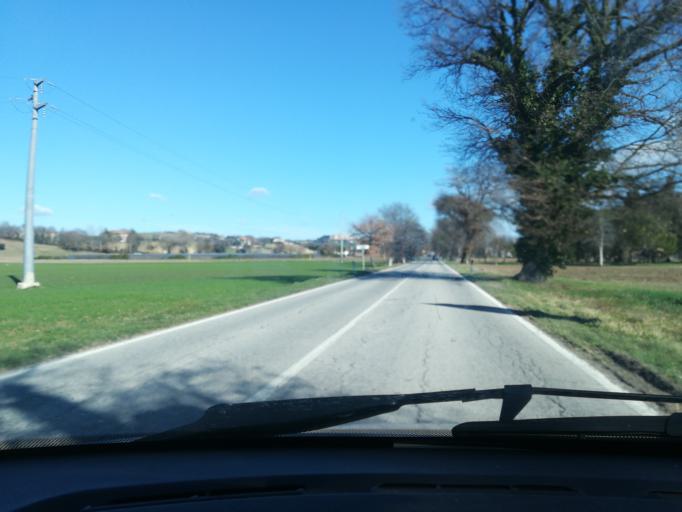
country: IT
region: The Marches
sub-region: Provincia di Macerata
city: Villa Potenza
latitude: 43.3338
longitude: 13.4268
